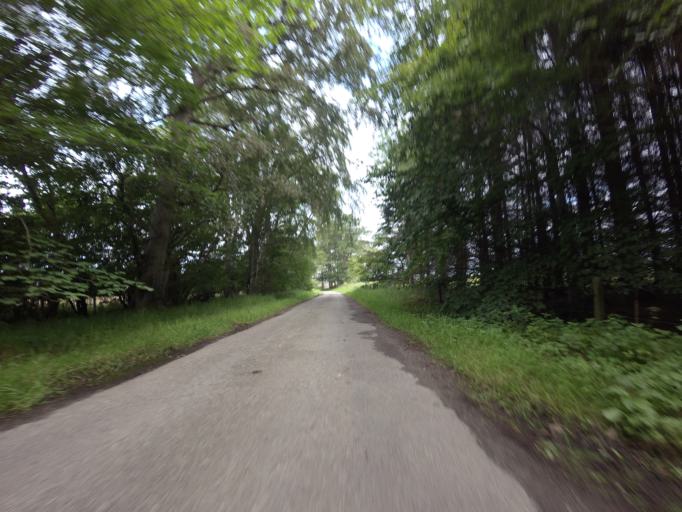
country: GB
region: Scotland
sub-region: Moray
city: Hopeman
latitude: 57.6719
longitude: -3.3996
